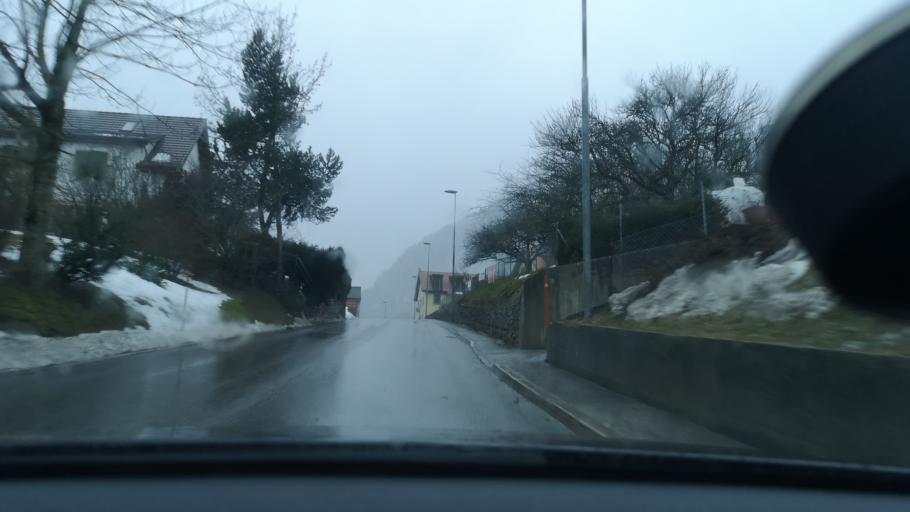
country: CH
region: Neuchatel
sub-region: Boudry District
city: Boudry
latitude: 46.9770
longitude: 6.8088
